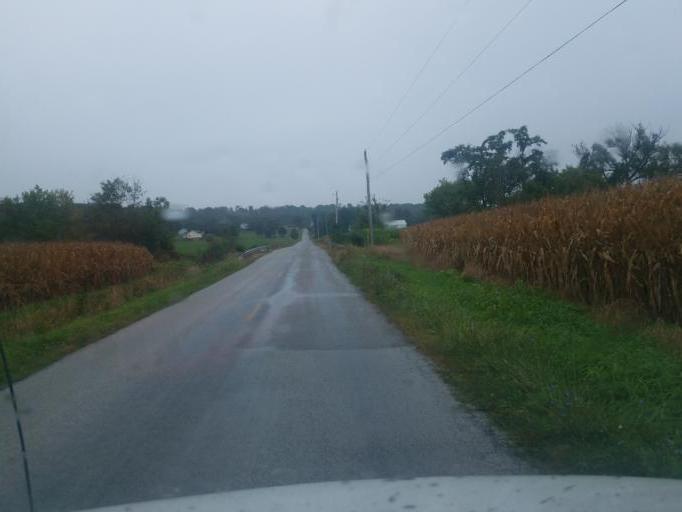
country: US
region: Ohio
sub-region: Medina County
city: Seville
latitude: 40.9824
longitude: -81.8490
